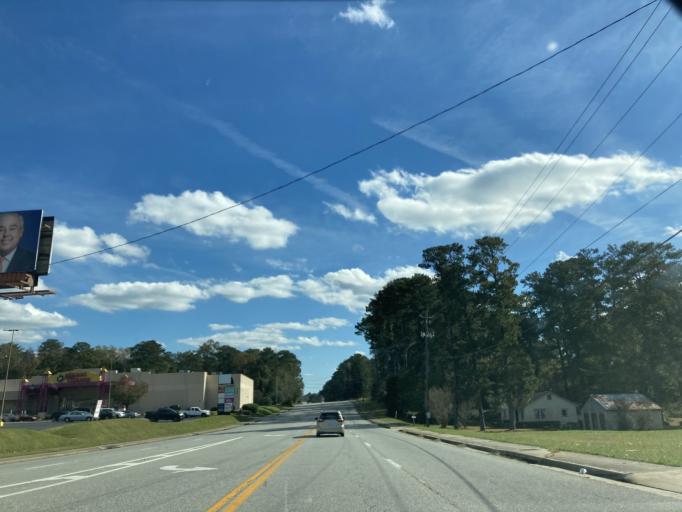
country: US
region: Georgia
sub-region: Bibb County
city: Macon
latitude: 32.8961
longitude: -83.6895
